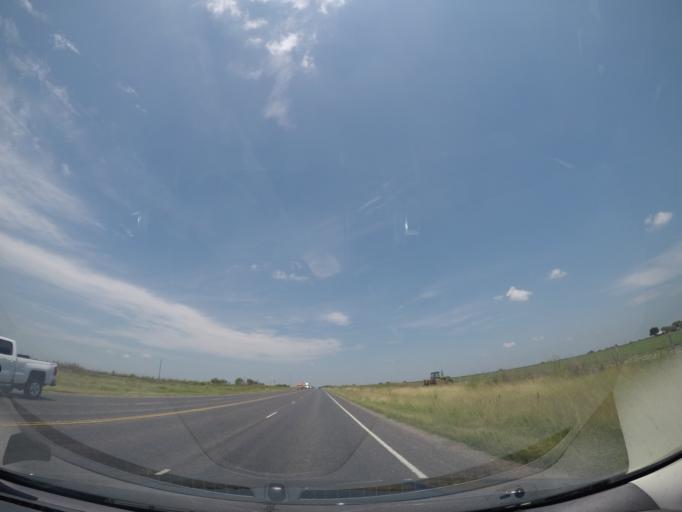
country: US
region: Texas
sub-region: Uvalde County
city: Sabinal
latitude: 29.3006
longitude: -99.6185
